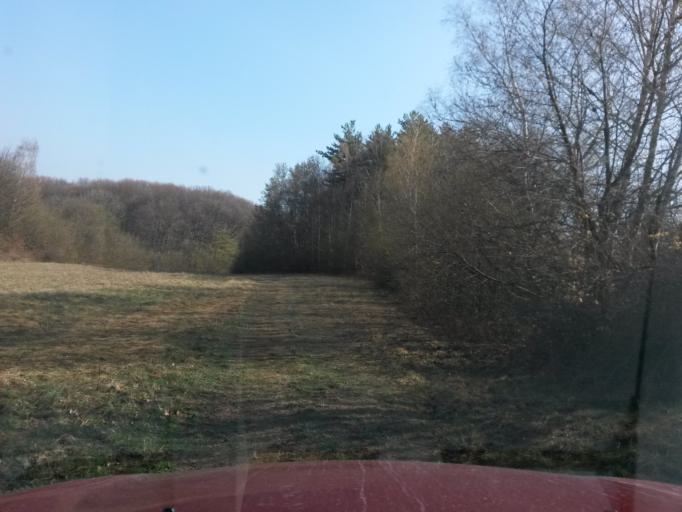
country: SK
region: Presovsky
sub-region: Okres Presov
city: Presov
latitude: 48.9279
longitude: 21.1467
